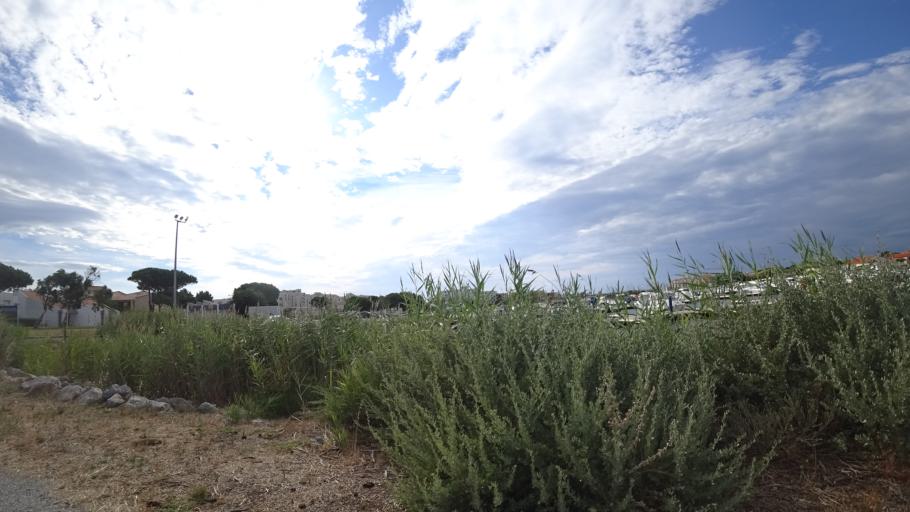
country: FR
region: Languedoc-Roussillon
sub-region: Departement des Pyrenees-Orientales
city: Le Barcares
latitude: 42.8008
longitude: 3.0335
